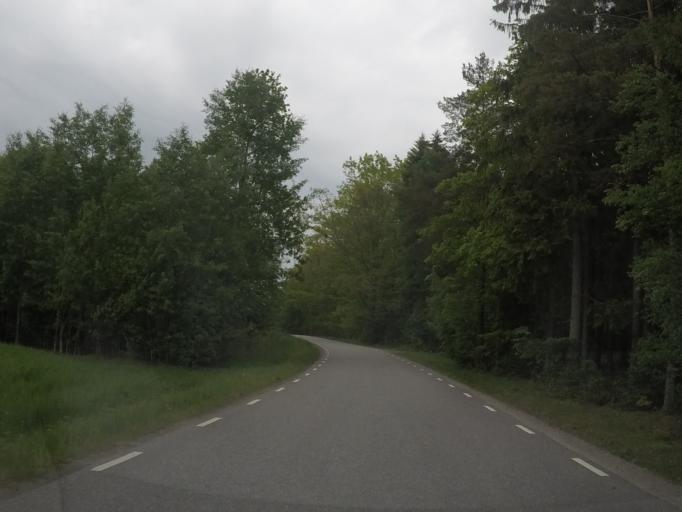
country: SE
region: Soedermanland
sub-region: Nykopings Kommun
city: Svalsta
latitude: 58.8167
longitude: 16.9008
